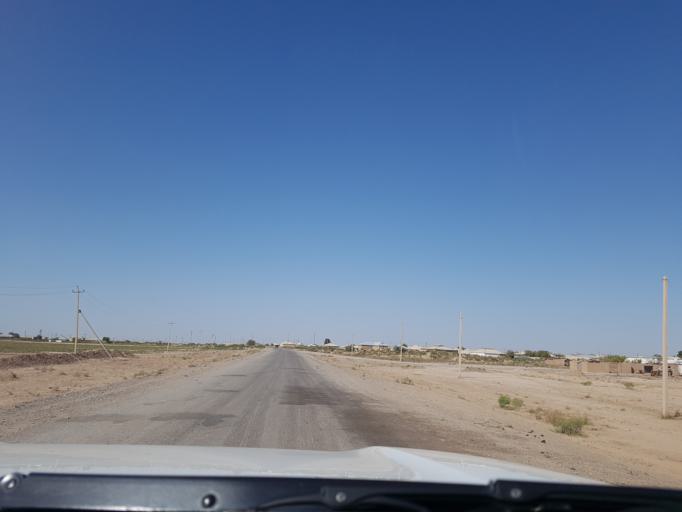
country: IR
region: Razavi Khorasan
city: Sarakhs
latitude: 36.5111
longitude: 61.2532
